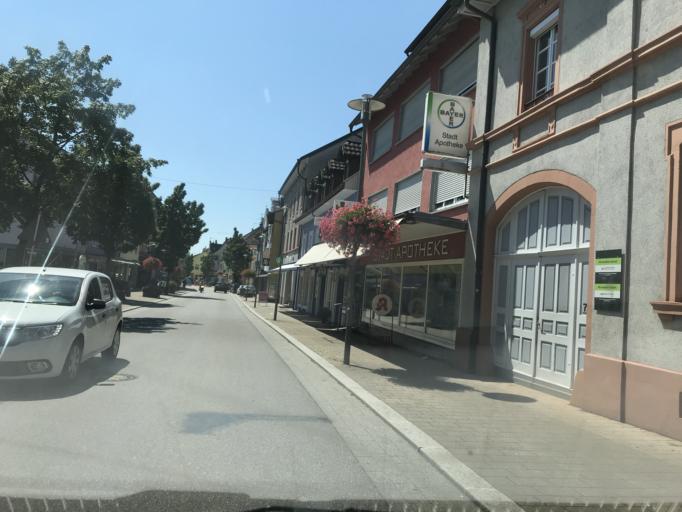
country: DE
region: Baden-Wuerttemberg
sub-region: Freiburg Region
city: Wehr
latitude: 47.6297
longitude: 7.9045
